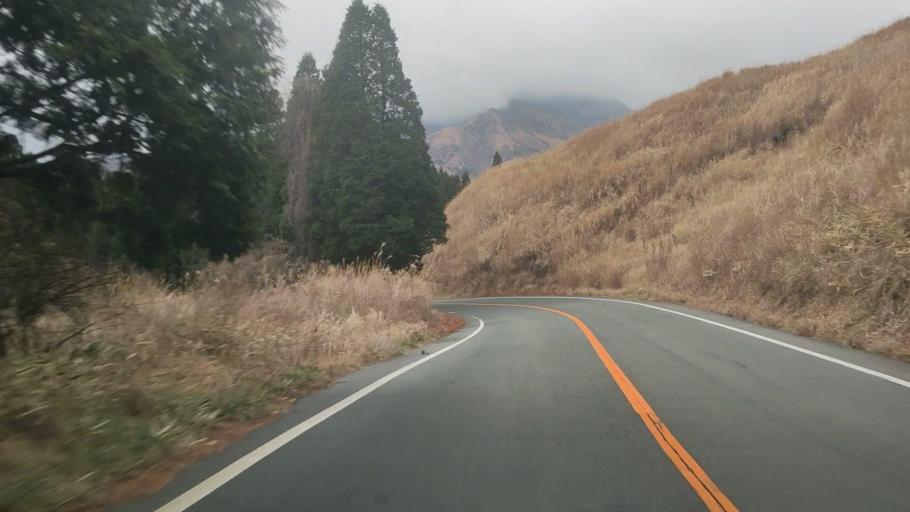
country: JP
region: Kumamoto
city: Aso
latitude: 32.9094
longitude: 131.1423
